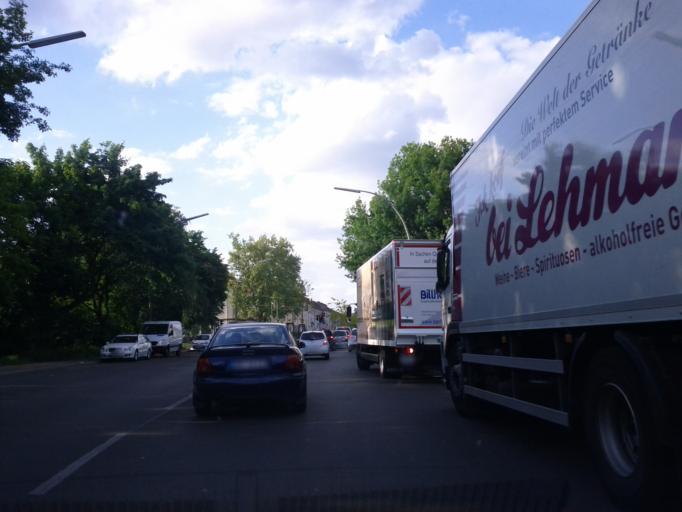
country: DE
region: Berlin
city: Wilhelmstadt
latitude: 52.5408
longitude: 13.1834
